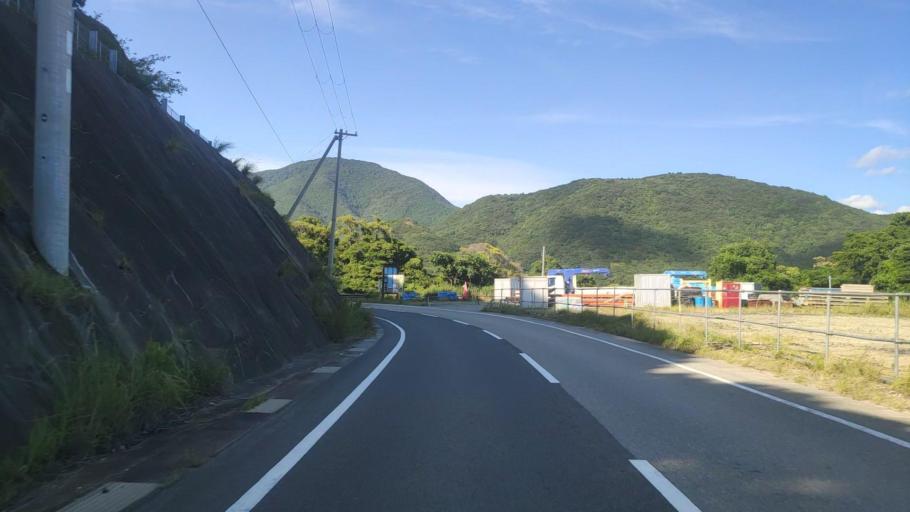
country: JP
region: Wakayama
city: Tanabe
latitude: 33.5096
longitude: 135.6021
